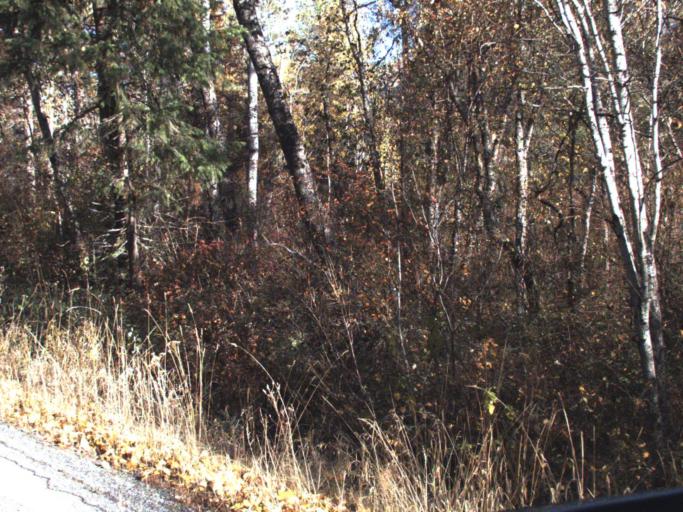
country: US
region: Washington
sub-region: Ferry County
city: Republic
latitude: 48.4335
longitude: -118.7334
